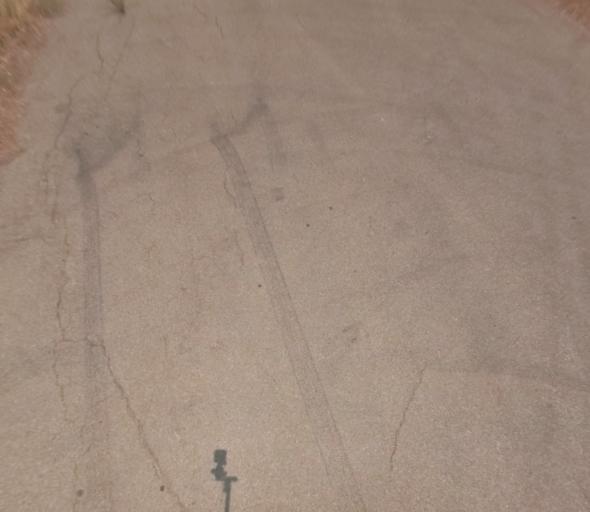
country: US
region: California
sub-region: Madera County
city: Oakhurst
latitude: 37.2517
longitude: -119.5725
